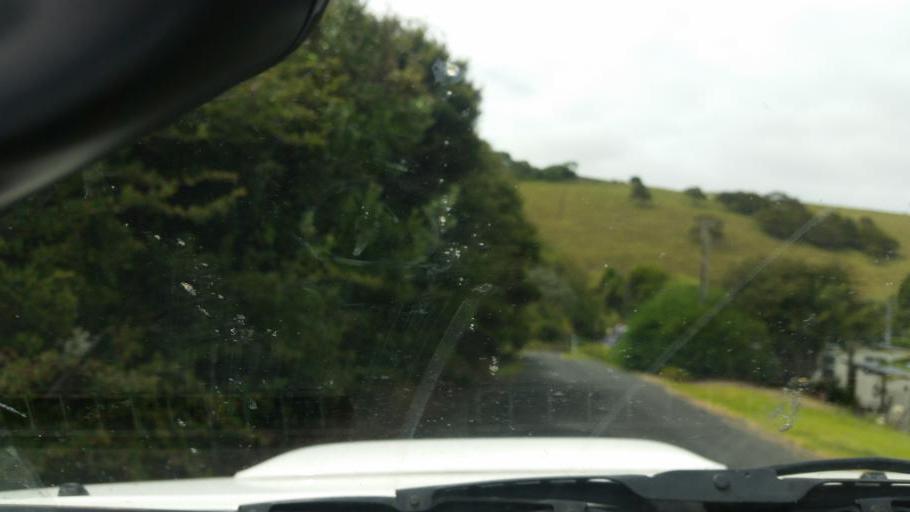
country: NZ
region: Auckland
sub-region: Auckland
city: Wellsford
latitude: -36.1571
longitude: 174.2383
